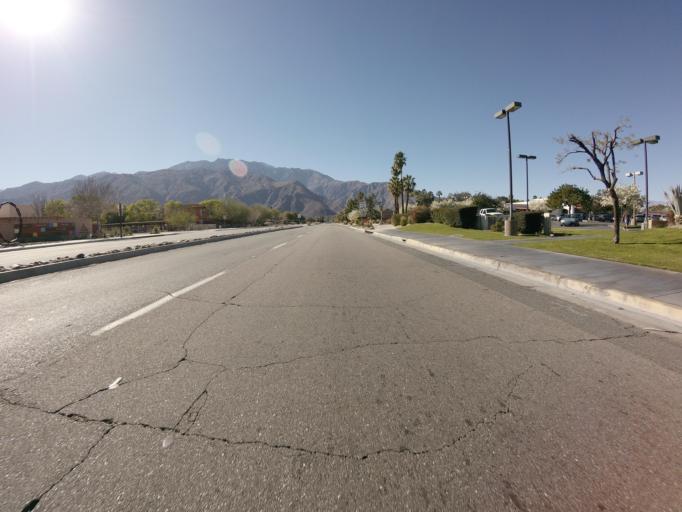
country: US
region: California
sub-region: Riverside County
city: Palm Springs
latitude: 33.8450
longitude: -116.5286
